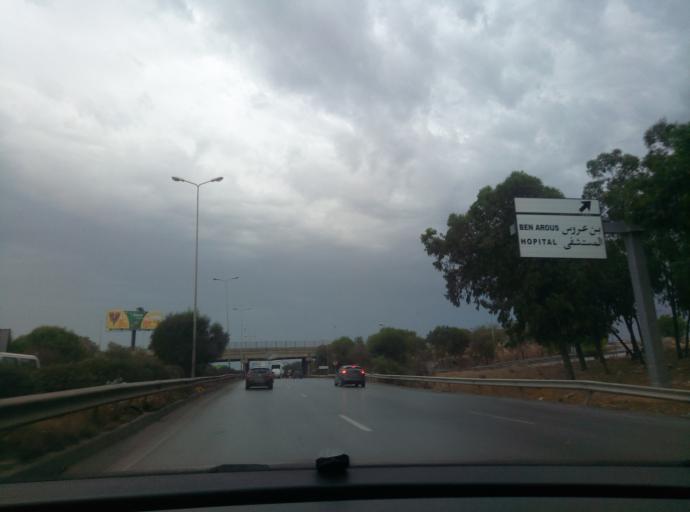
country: TN
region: Bin 'Arus
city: Ben Arous
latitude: 36.7476
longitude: 10.2086
